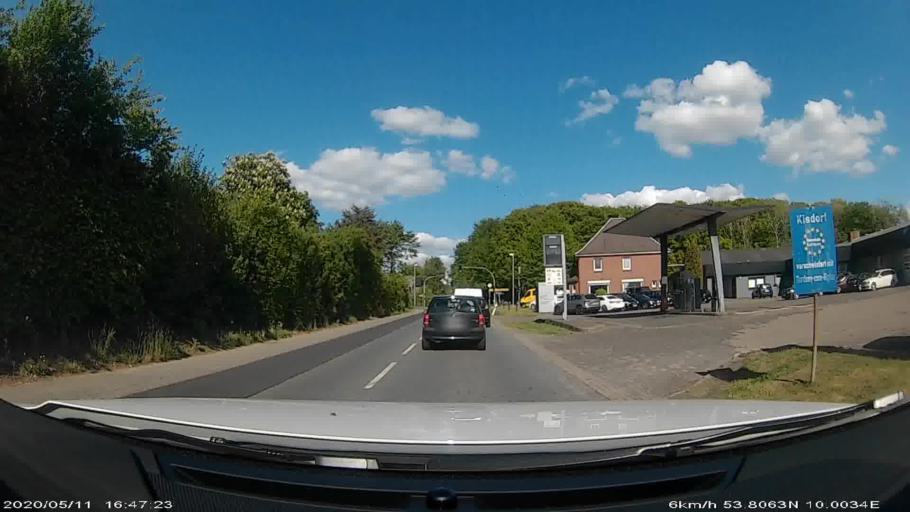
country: DE
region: Schleswig-Holstein
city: Kisdorf
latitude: 53.8148
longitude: 9.9984
